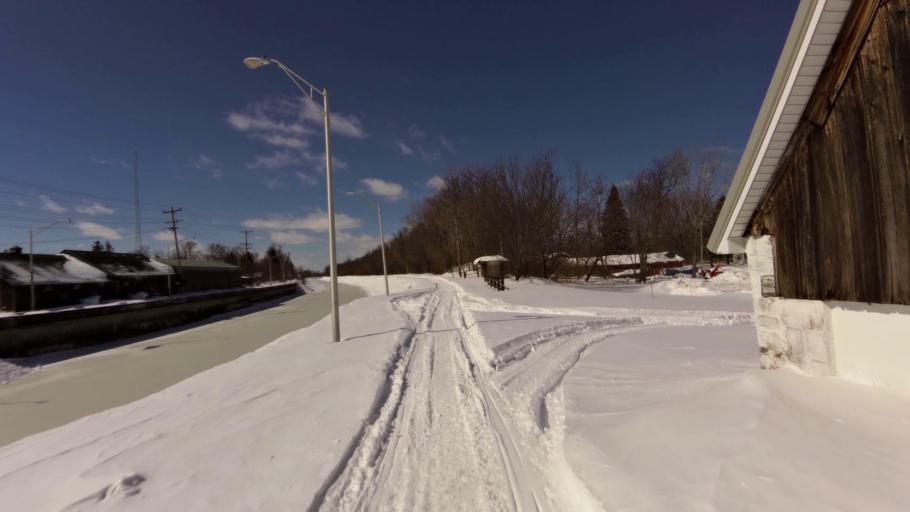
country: US
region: New York
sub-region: Orleans County
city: Albion
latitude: 43.2493
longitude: -78.1945
